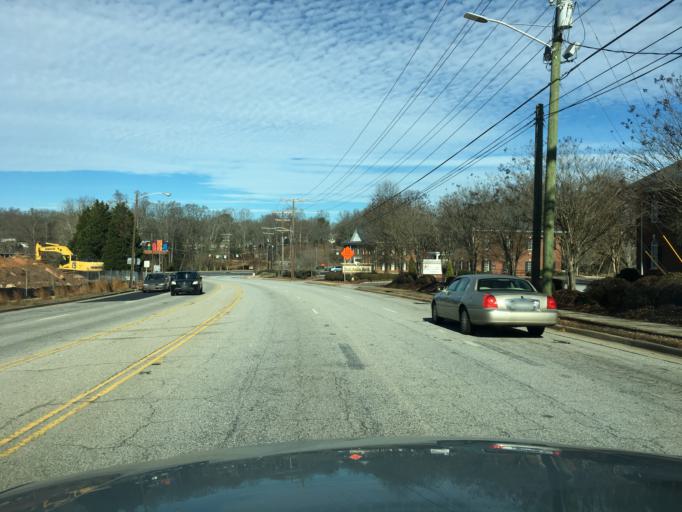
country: US
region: South Carolina
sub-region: Greenville County
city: Greenville
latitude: 34.8606
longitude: -82.3849
